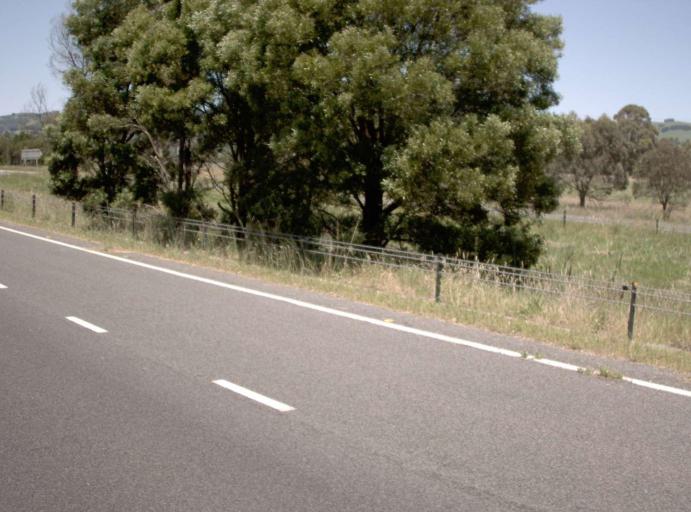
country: AU
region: Victoria
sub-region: Baw Baw
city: Warragul
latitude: -38.1994
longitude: 146.0431
